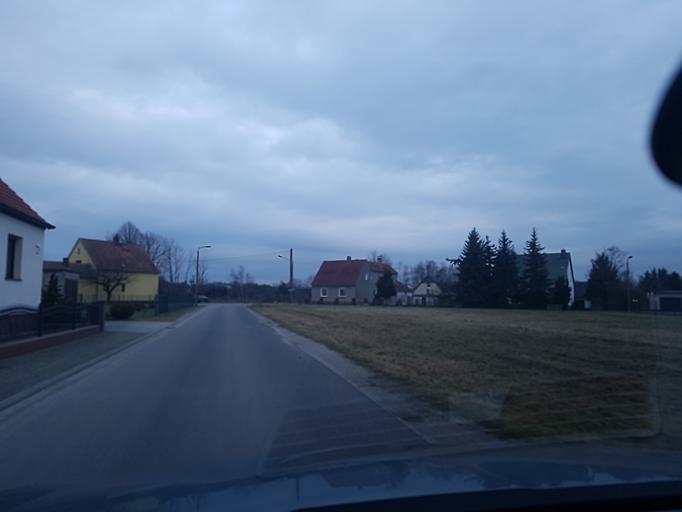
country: DE
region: Brandenburg
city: Doberlug-Kirchhain
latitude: 51.6078
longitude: 13.5597
